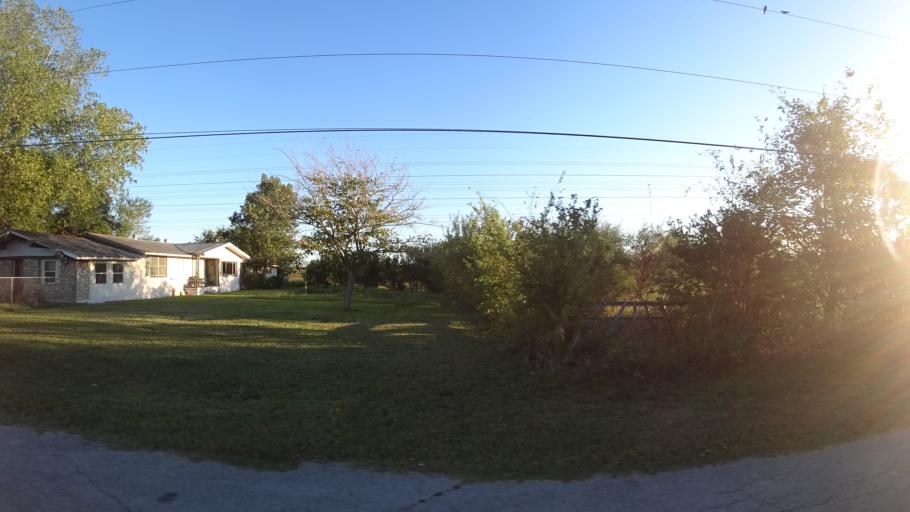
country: US
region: Texas
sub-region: Travis County
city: Hornsby Bend
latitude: 30.3076
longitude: -97.6198
